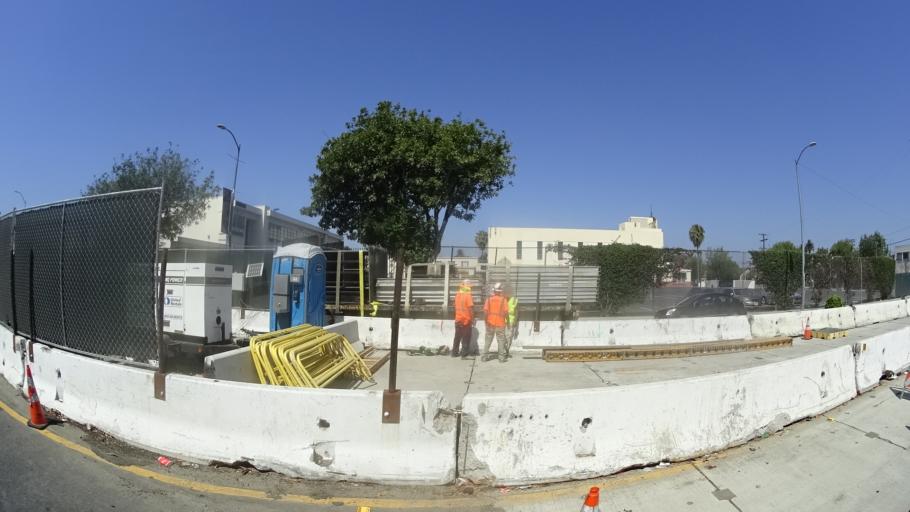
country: US
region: California
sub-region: Los Angeles County
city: View Park-Windsor Hills
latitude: 33.9848
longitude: -118.3309
